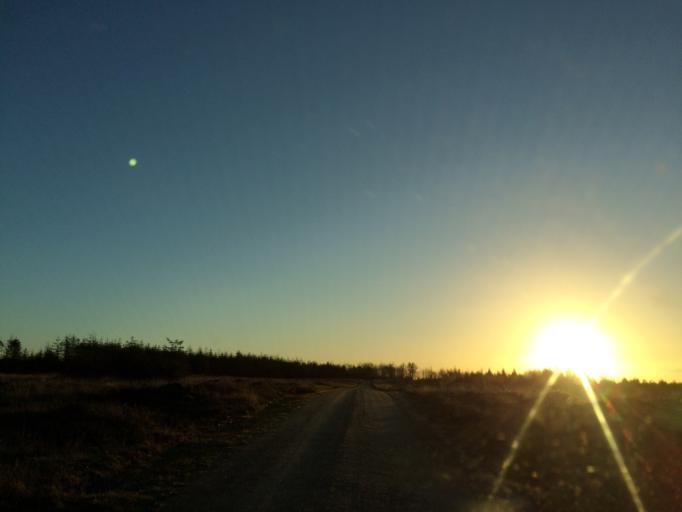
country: DK
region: Central Jutland
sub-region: Holstebro Kommune
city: Holstebro
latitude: 56.2193
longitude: 8.5156
